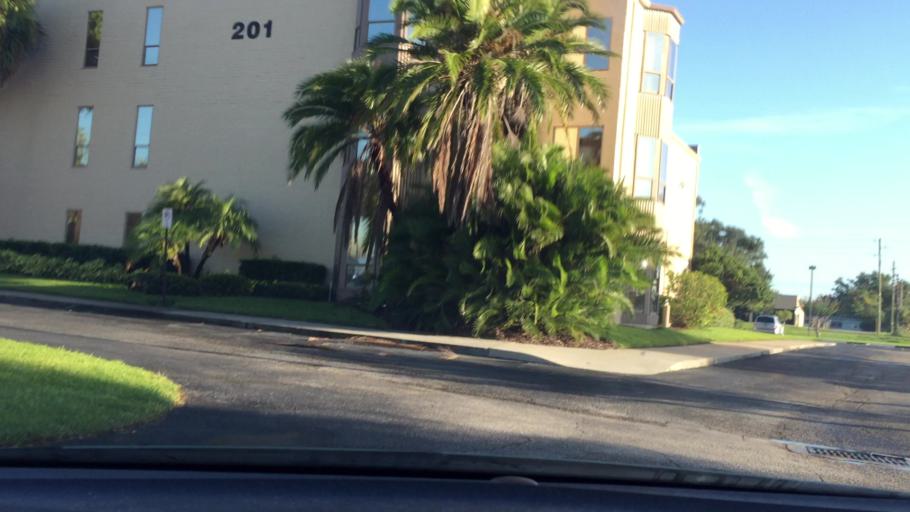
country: US
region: Florida
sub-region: Osceola County
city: Kissimmee
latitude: 28.3176
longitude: -81.4057
